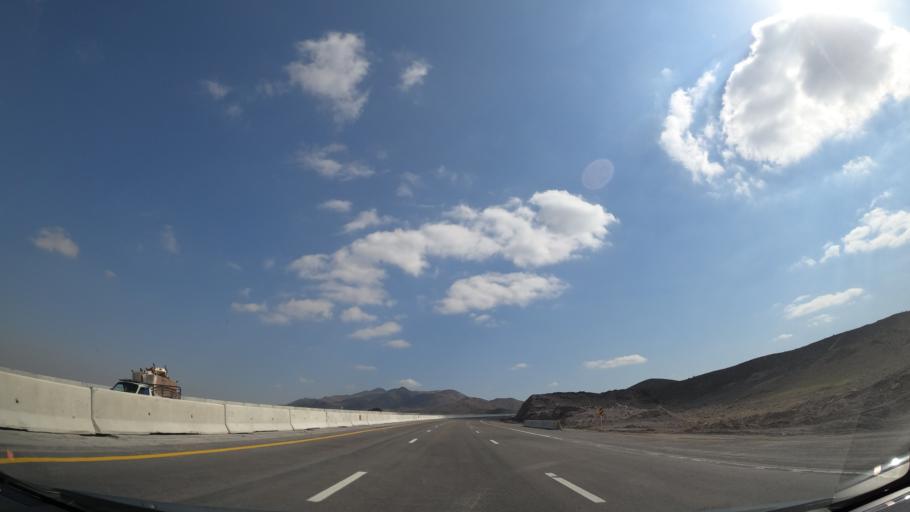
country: IR
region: Alborz
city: Nazarabad
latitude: 35.6964
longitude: 50.6290
